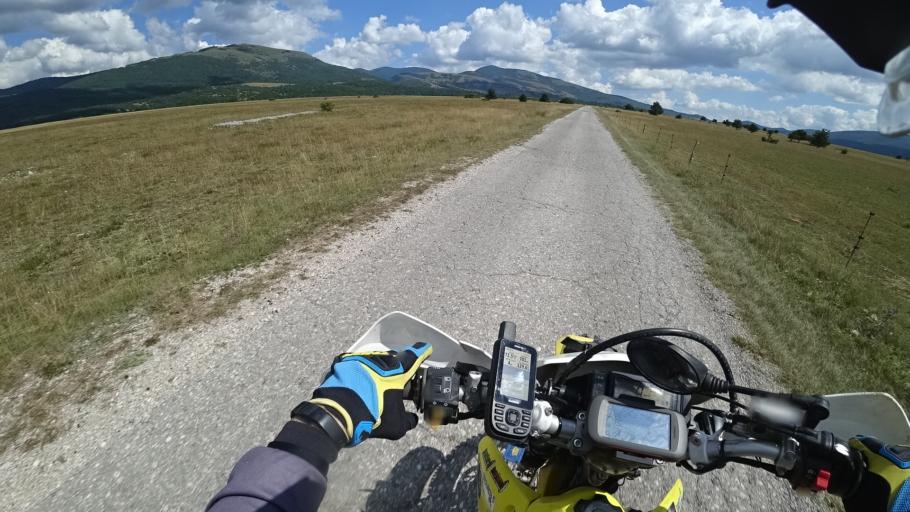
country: HR
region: Zadarska
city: Gracac
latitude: 44.5434
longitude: 15.7873
